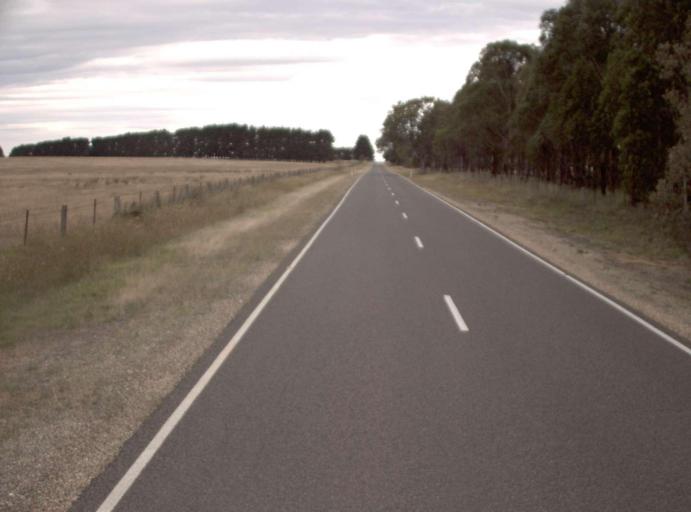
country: AU
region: Victoria
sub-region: East Gippsland
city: Bairnsdale
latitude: -37.9677
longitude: 147.4807
